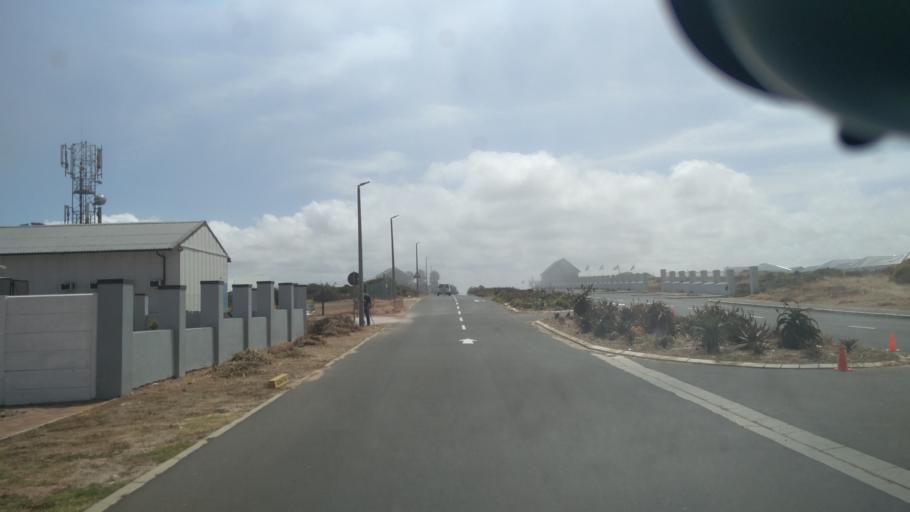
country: ZA
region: Western Cape
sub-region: City of Cape Town
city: Atlantis
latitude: -33.3487
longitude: 18.1556
